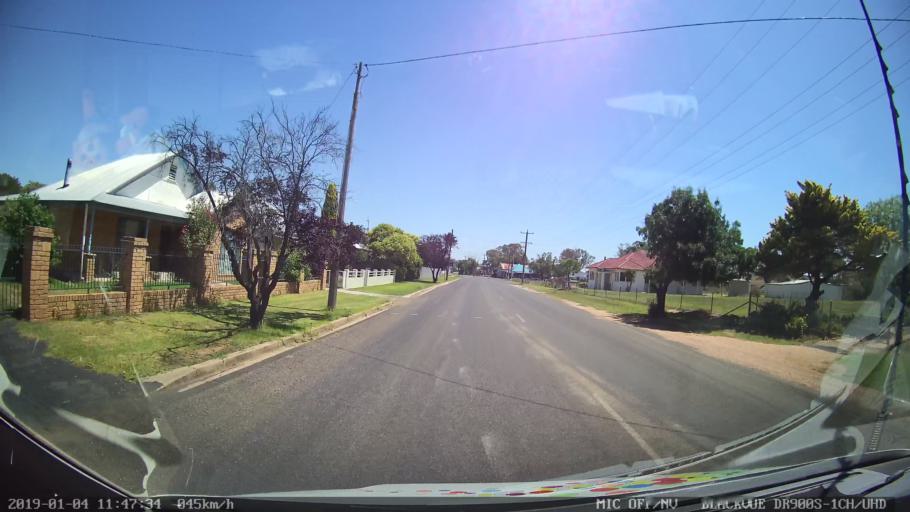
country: AU
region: New South Wales
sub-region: Cabonne
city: Molong
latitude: -32.9319
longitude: 148.7548
